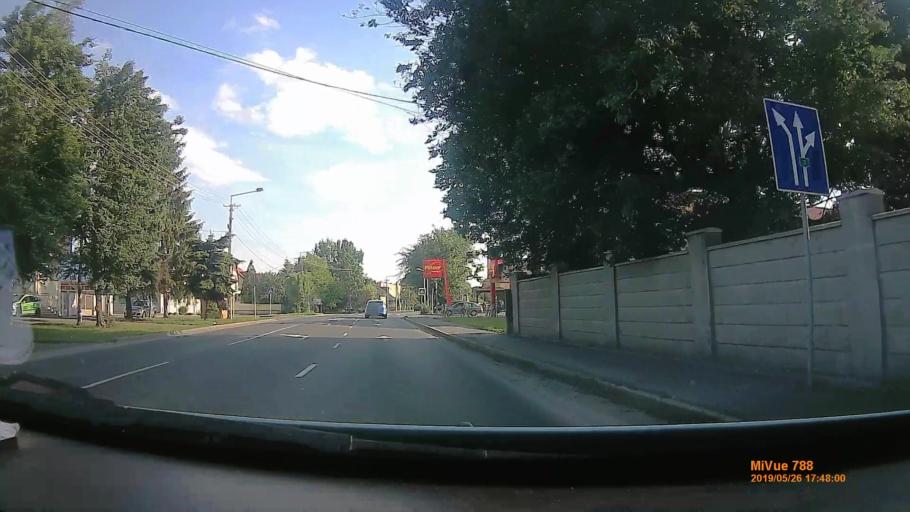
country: HU
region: Borsod-Abauj-Zemplen
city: Szikszo
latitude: 48.1983
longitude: 20.9313
